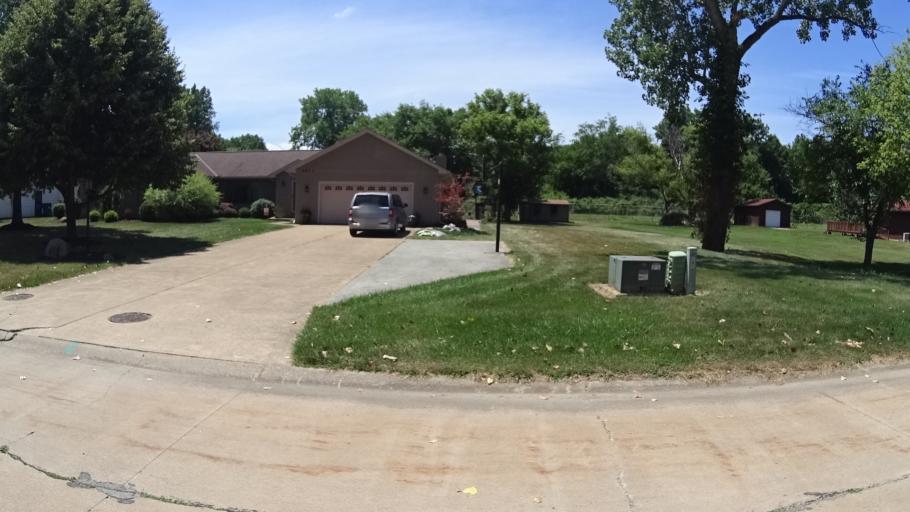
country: US
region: Ohio
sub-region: Erie County
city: Sandusky
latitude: 41.3909
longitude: -82.6732
